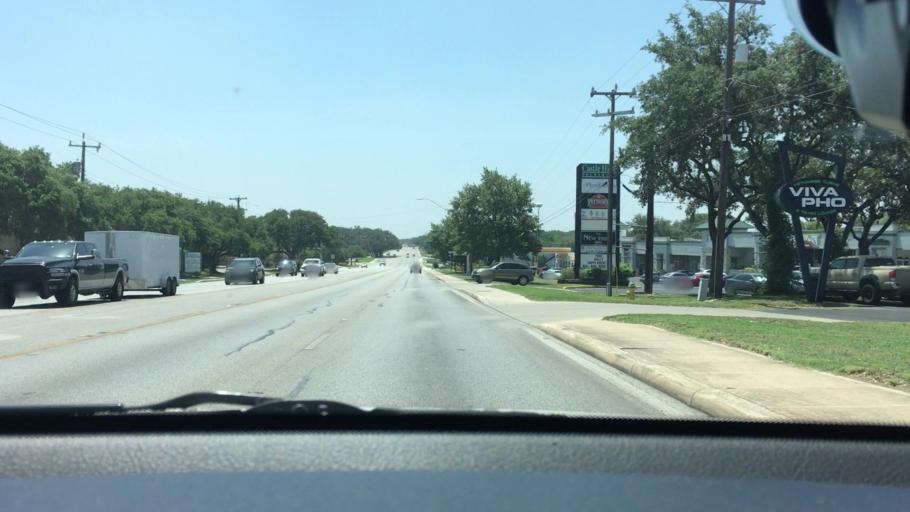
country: US
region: Texas
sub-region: Bexar County
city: Castle Hills
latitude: 29.5317
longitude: -98.5219
